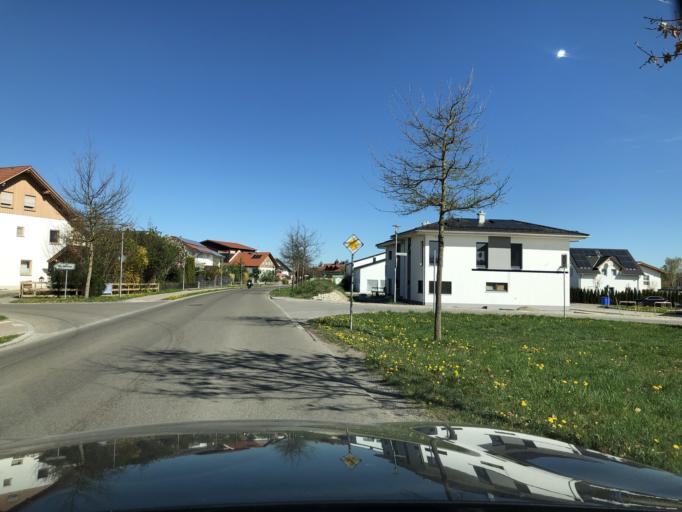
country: DE
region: Bavaria
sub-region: Swabia
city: Wald
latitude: 47.7444
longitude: 10.5763
